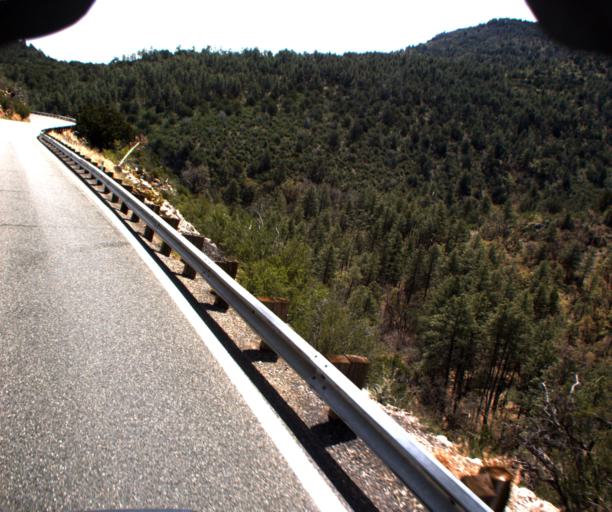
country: US
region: Arizona
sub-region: Yavapai County
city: Clarkdale
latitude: 34.7220
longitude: -112.1497
